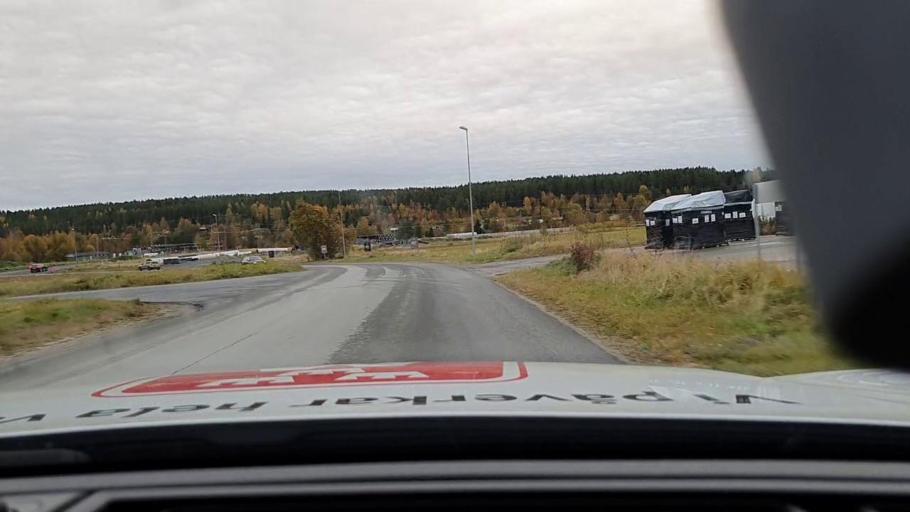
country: SE
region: Norrbotten
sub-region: Bodens Kommun
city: Saevast
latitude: 65.7548
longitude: 21.7598
